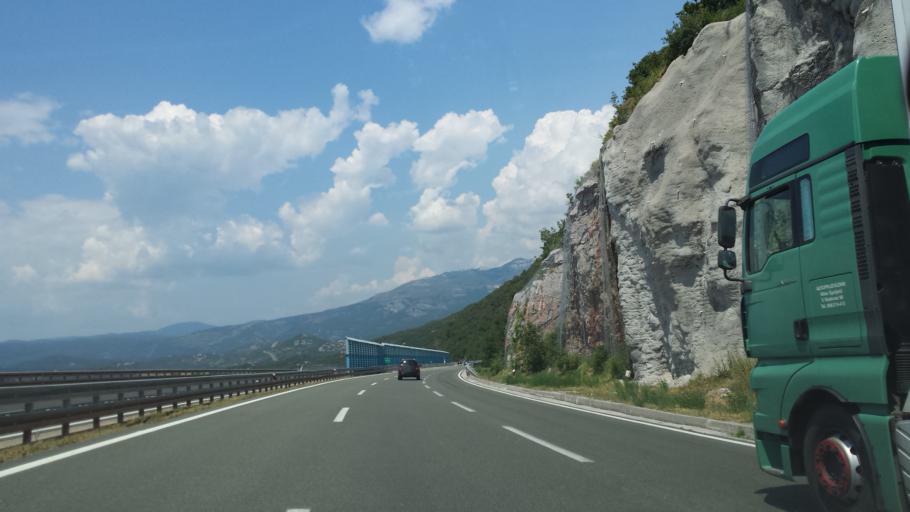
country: HR
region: Primorsko-Goranska
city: Skrljevo
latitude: 45.3635
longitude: 14.5522
